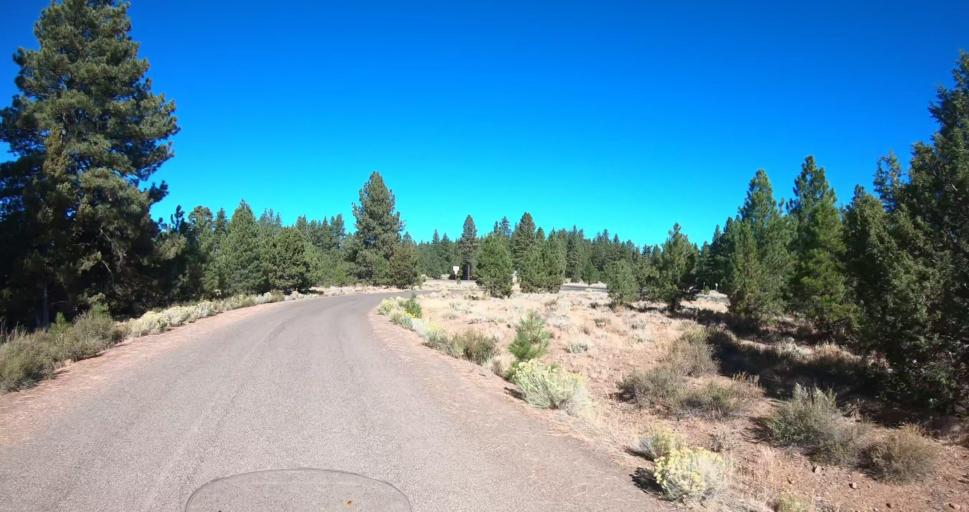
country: US
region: Oregon
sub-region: Lake County
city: Lakeview
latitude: 42.2245
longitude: -120.2305
